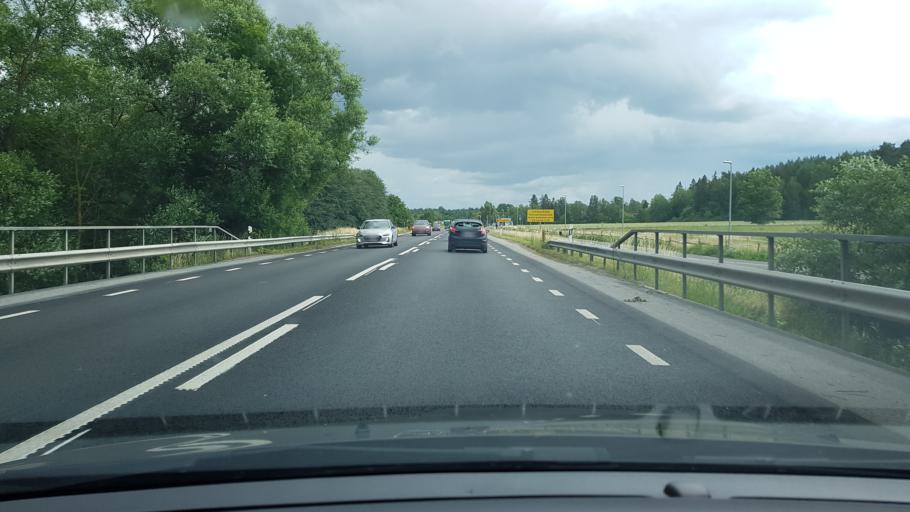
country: SE
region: Uppsala
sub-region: Uppsala Kommun
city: Saevja
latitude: 59.8318
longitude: 17.6911
